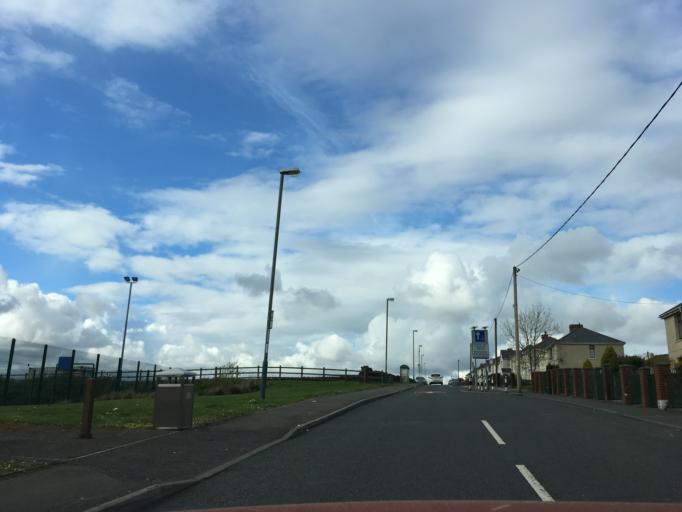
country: GB
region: Wales
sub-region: Caerphilly County Borough
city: Rhymney
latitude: 51.7429
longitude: -3.2953
